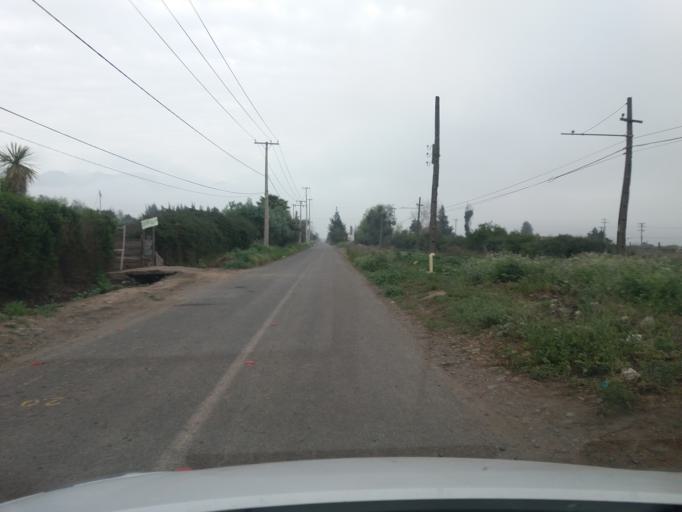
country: CL
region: Valparaiso
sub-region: Provincia de San Felipe
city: Llaillay
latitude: -32.8400
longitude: -71.0618
